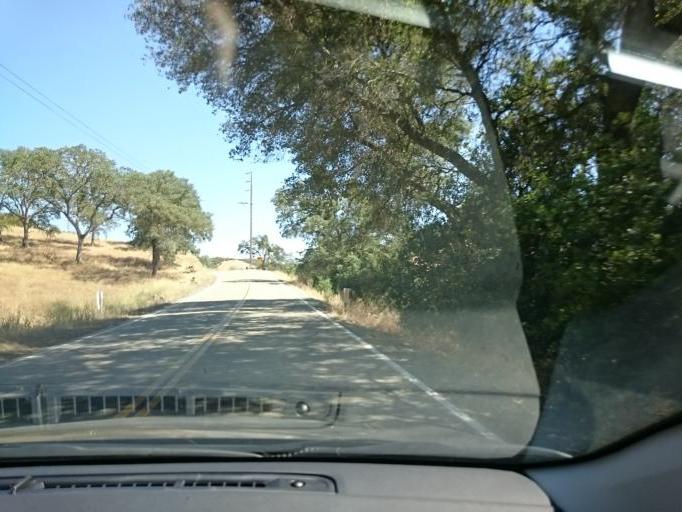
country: US
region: California
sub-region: Calaveras County
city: Rancho Calaveras
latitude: 38.1496
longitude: -120.8300
